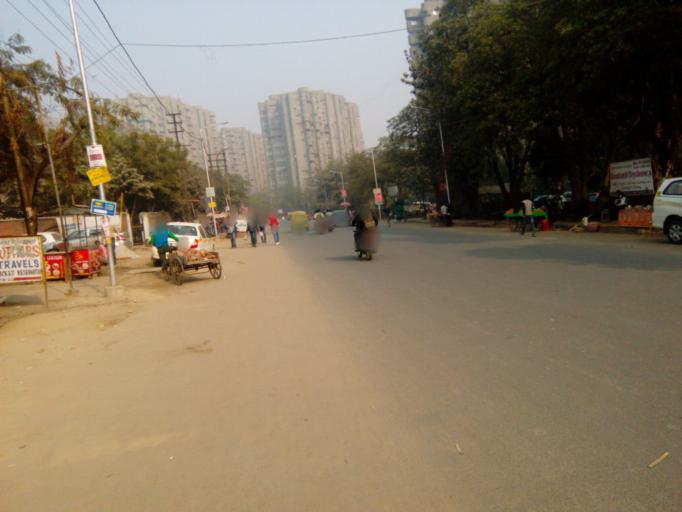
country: IN
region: Uttar Pradesh
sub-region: Gautam Buddha Nagar
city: Noida
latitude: 28.6416
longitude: 77.3194
